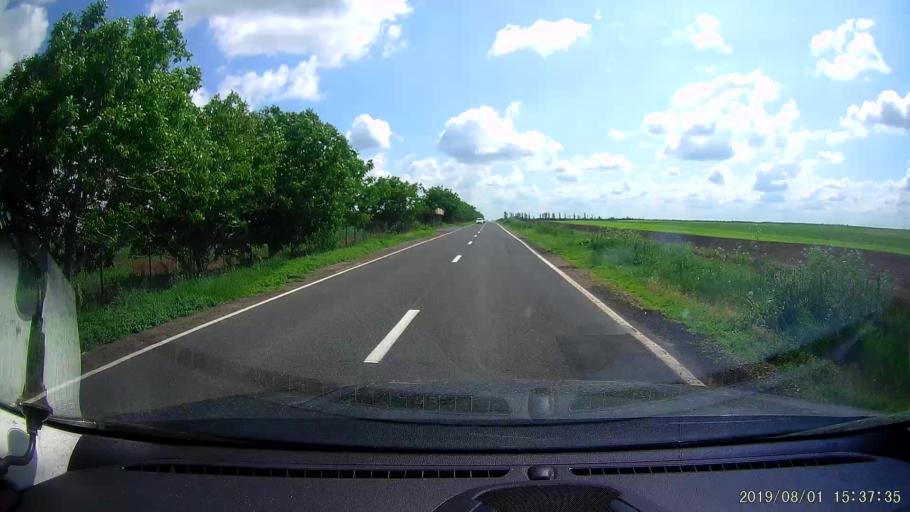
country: RO
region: Braila
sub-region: Comuna Insuratei
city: Insuratei
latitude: 44.9004
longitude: 27.5876
